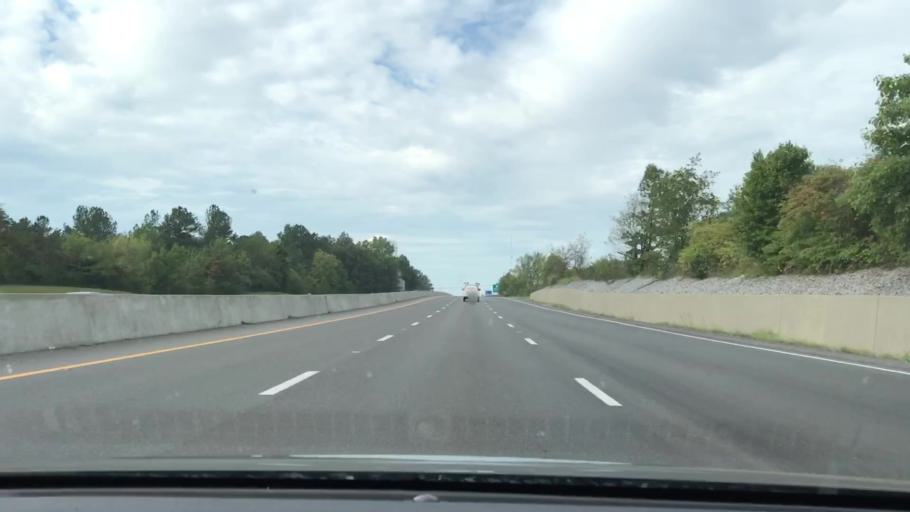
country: US
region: Kentucky
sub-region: Graves County
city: Mayfield
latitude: 36.7656
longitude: -88.6453
